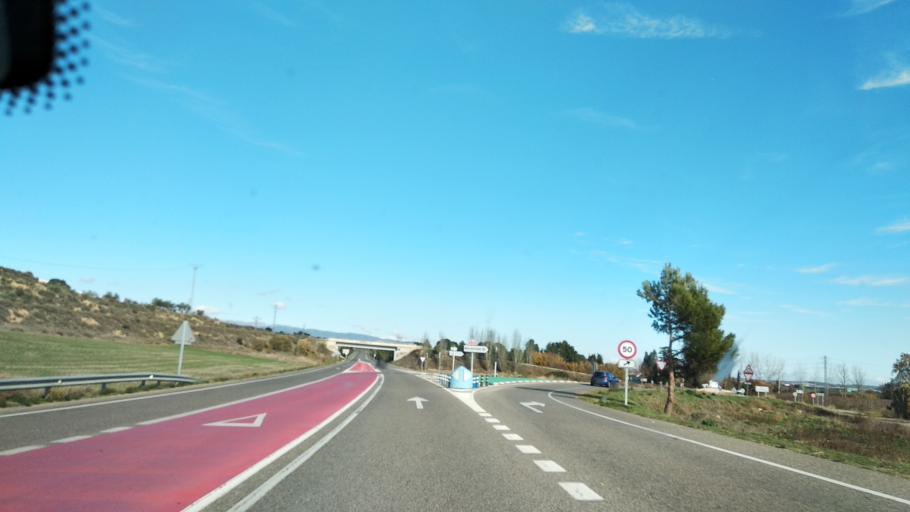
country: ES
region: Catalonia
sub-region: Provincia de Lleida
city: Vallfogona de Balaguer
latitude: 41.7674
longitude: 0.7864
